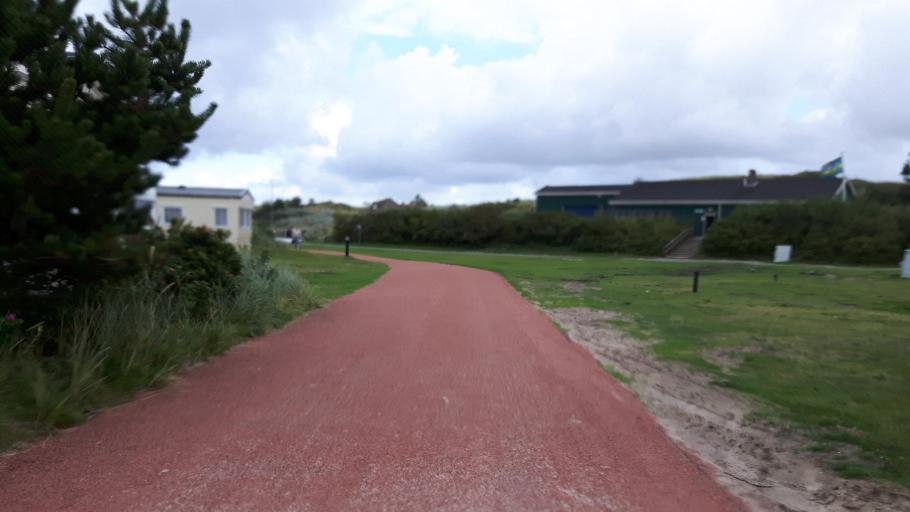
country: NL
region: Friesland
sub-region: Gemeente Ameland
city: Nes
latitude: 53.4572
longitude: 5.7697
